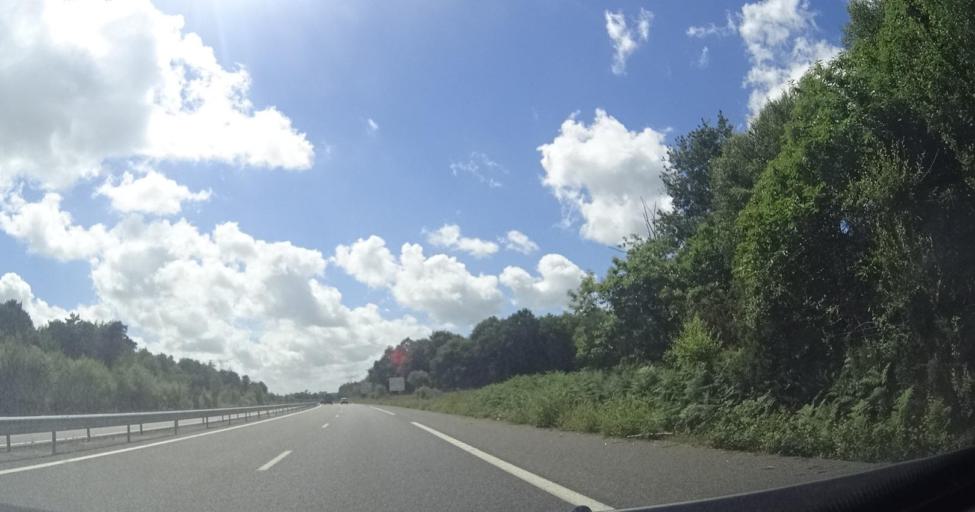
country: FR
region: Brittany
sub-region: Departement du Morbihan
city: Pluherlin
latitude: 47.6700
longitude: -2.3425
